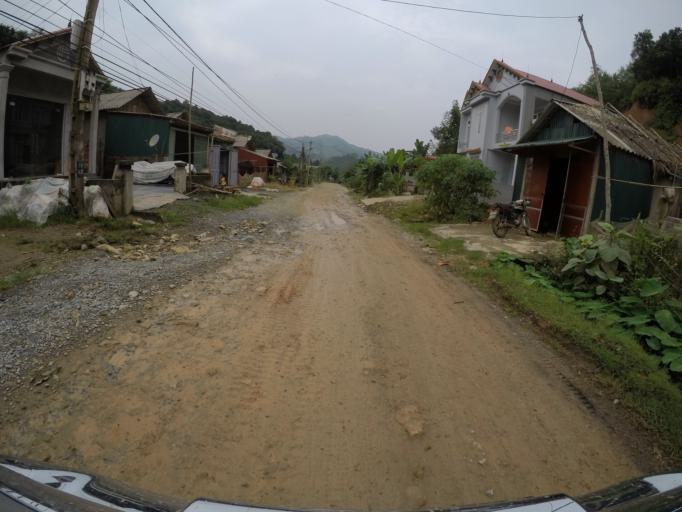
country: VN
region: Yen Bai
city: Co Phuc
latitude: 21.8615
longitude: 104.6330
